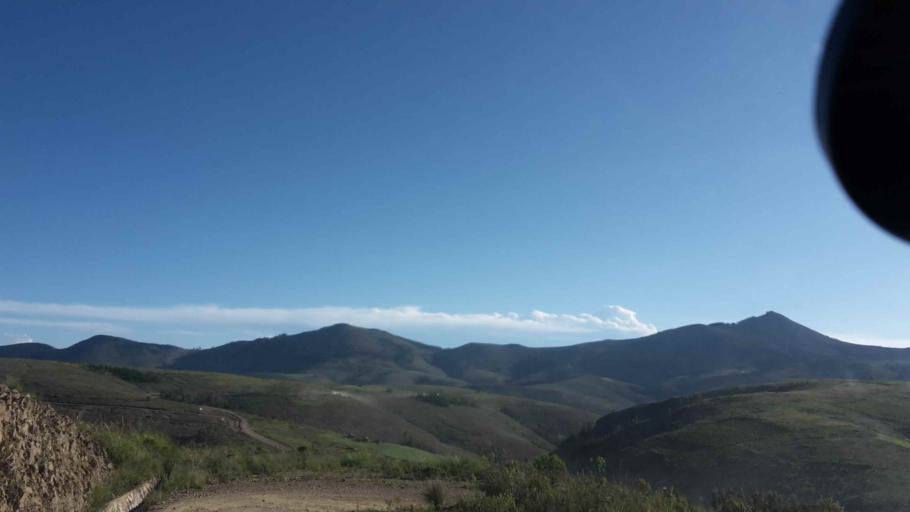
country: BO
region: Cochabamba
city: Arani
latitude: -17.7485
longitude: -65.6227
